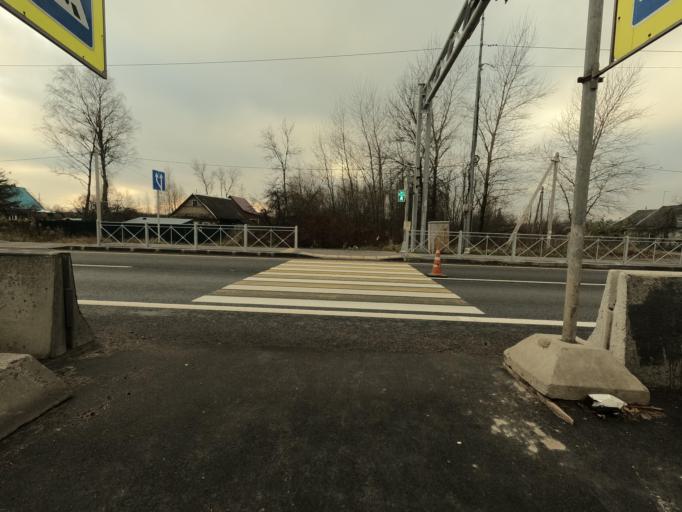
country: RU
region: Leningrad
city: Mga
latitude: 59.7181
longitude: 31.1076
